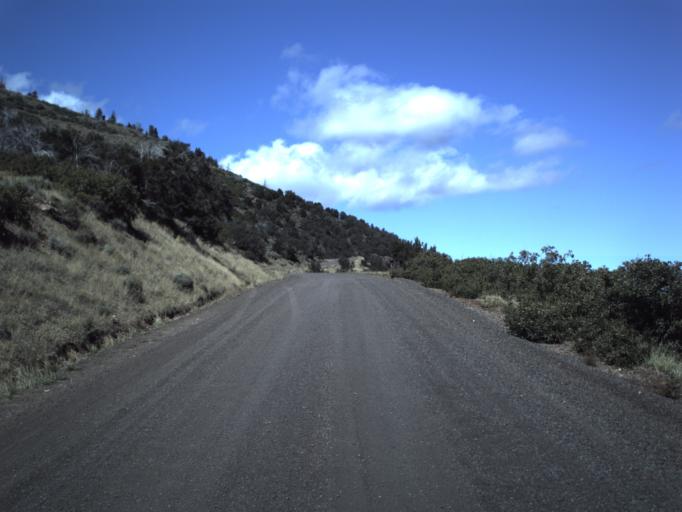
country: US
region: Utah
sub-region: Piute County
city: Junction
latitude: 38.2564
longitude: -112.3184
